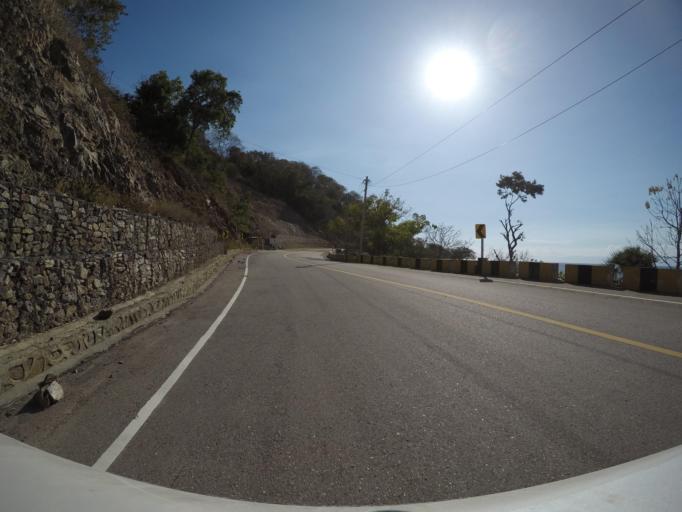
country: TL
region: Liquica
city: Maubara
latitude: -8.6382
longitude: 125.1346
